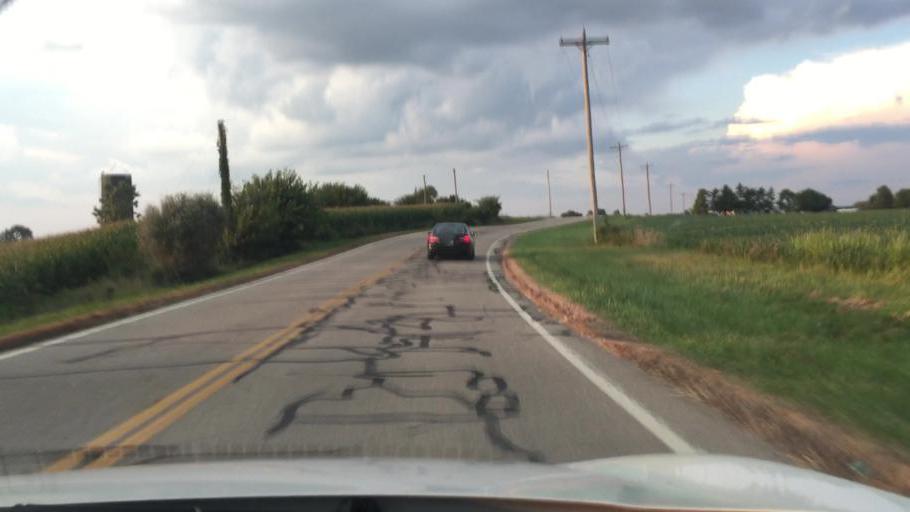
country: US
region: Ohio
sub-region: Champaign County
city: Mechanicsburg
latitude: 40.0331
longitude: -83.5726
